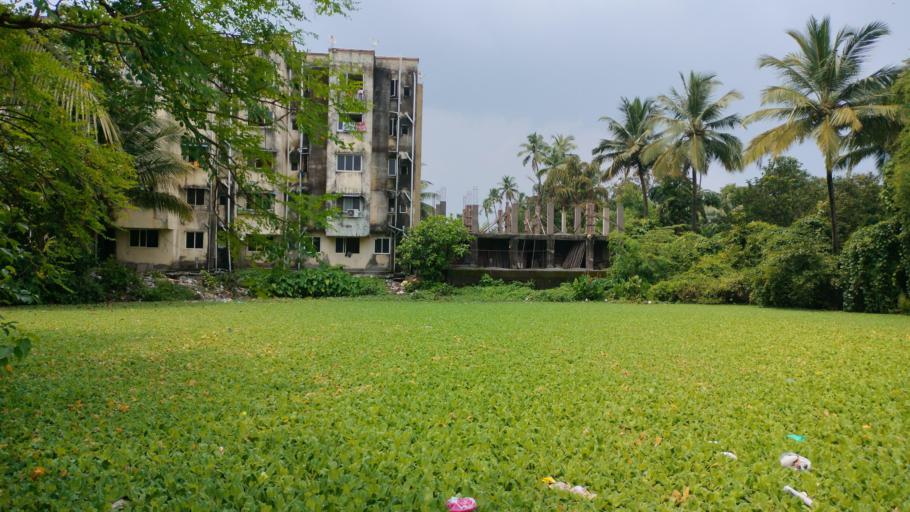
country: IN
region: Maharashtra
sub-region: Thane
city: Virar
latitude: 19.4102
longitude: 72.8043
